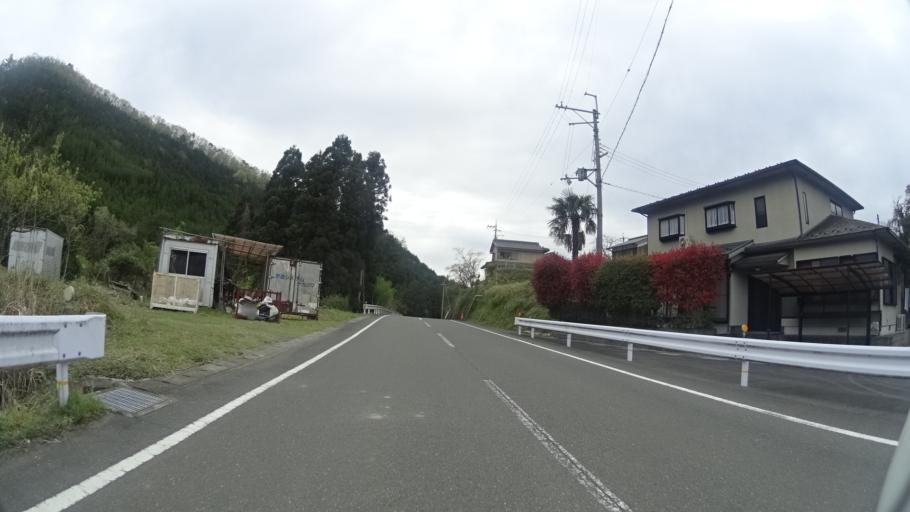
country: JP
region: Kyoto
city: Ayabe
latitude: 35.2167
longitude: 135.4674
